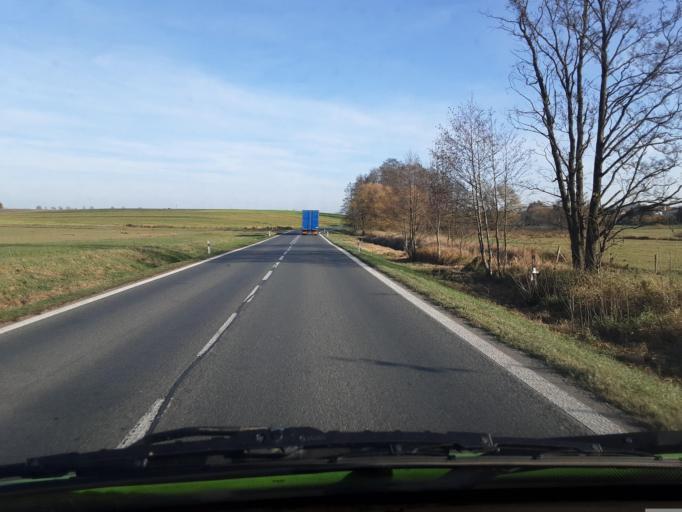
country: CZ
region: Plzensky
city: Horazd'ovice
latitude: 49.3284
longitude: 13.6711
